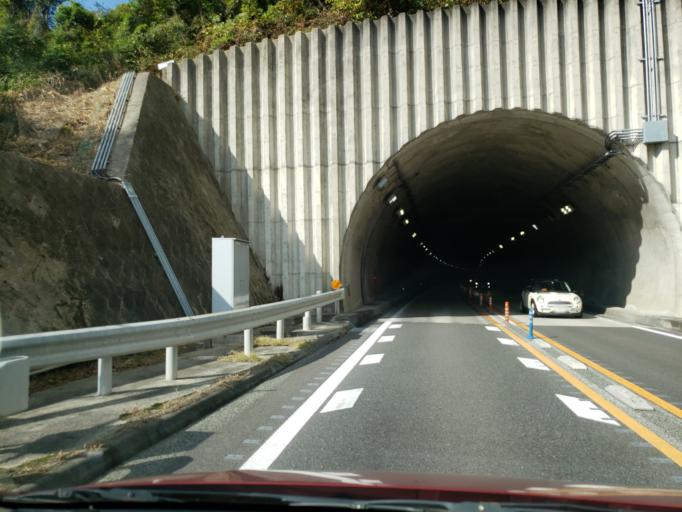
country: JP
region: Tokushima
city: Kamojimacho-jogejima
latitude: 34.1054
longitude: 134.2943
